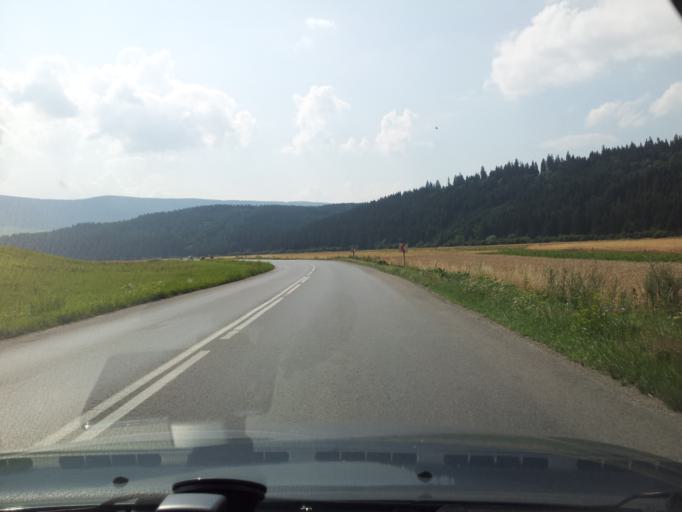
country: SK
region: Zilinsky
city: Namestovo
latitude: 49.3777
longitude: 19.3874
